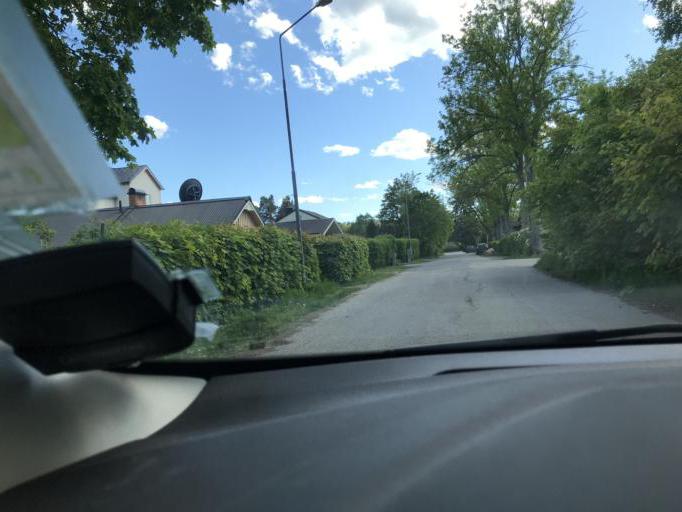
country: SE
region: Stockholm
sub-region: Botkyrka Kommun
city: Tumba
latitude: 59.1927
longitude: 17.8213
